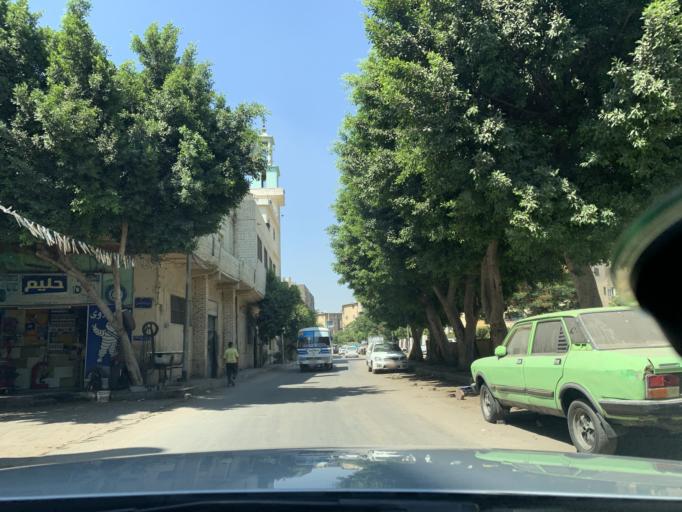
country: EG
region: Muhafazat al Qahirah
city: Cairo
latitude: 30.0717
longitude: 31.2560
